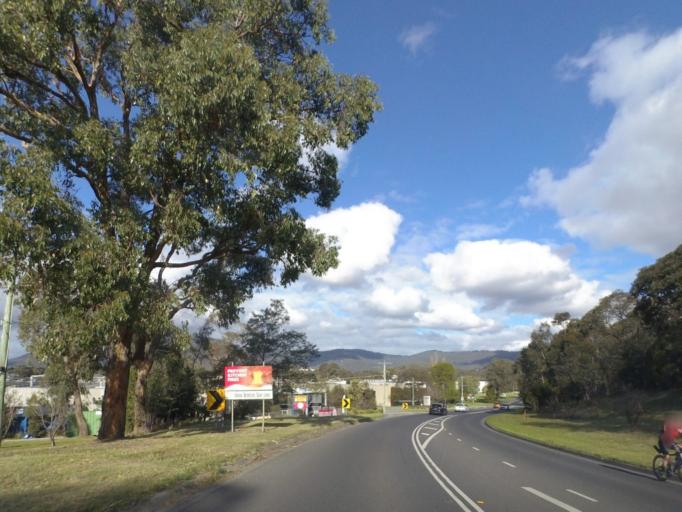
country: AU
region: Victoria
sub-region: Maroondah
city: Bayswater North
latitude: -37.8383
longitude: 145.2930
